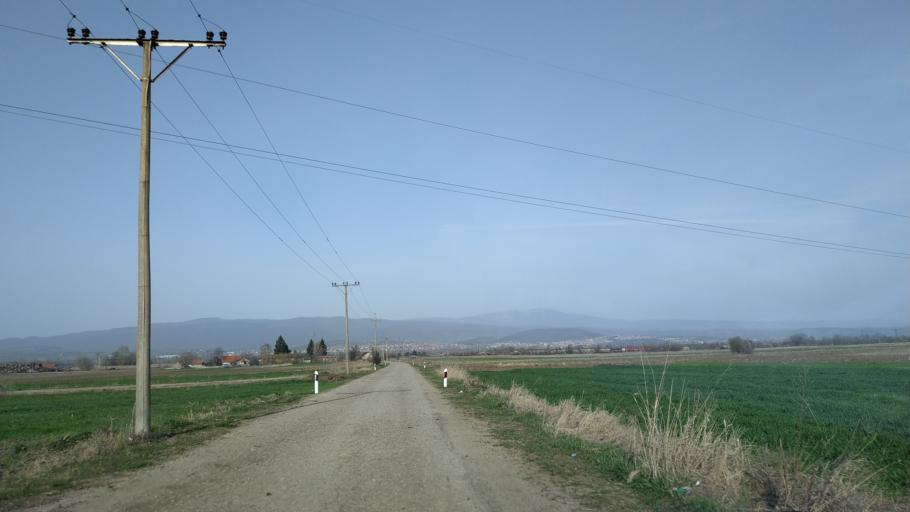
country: RS
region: Central Serbia
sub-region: Nisavski Okrug
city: Aleksinac
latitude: 43.5183
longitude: 21.6495
